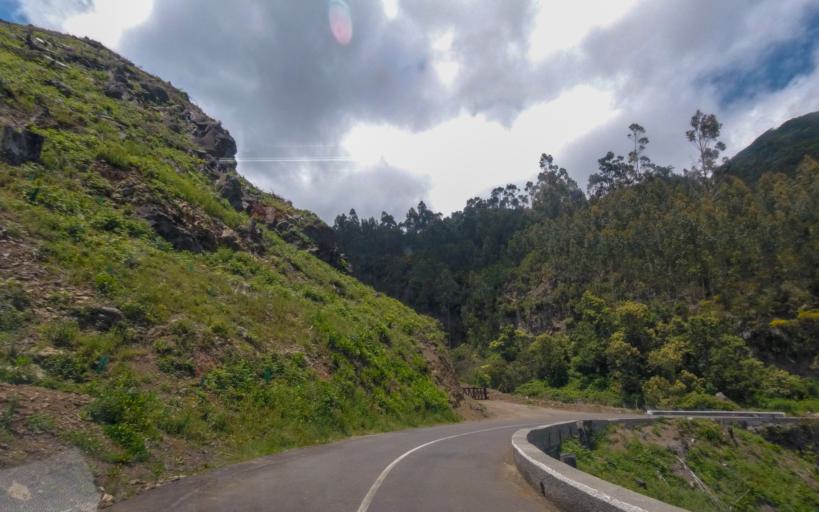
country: PT
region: Madeira
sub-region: Funchal
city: Nossa Senhora do Monte
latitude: 32.6922
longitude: -16.8972
